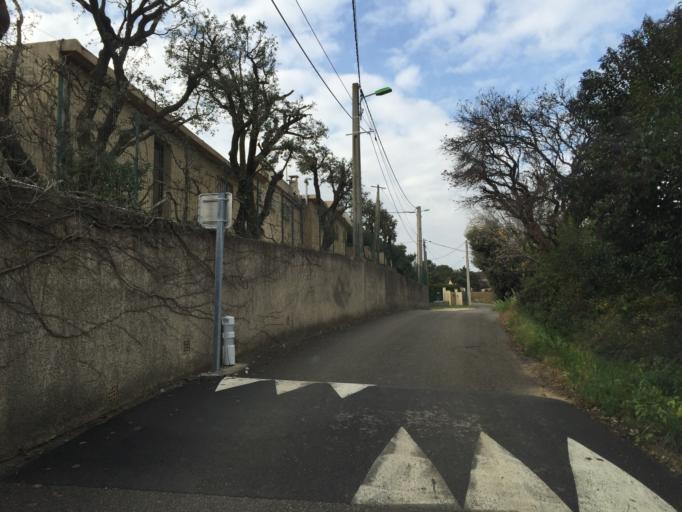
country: FR
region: Provence-Alpes-Cote d'Azur
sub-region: Departement du Vaucluse
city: Bedarrides
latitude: 44.0445
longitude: 4.8852
